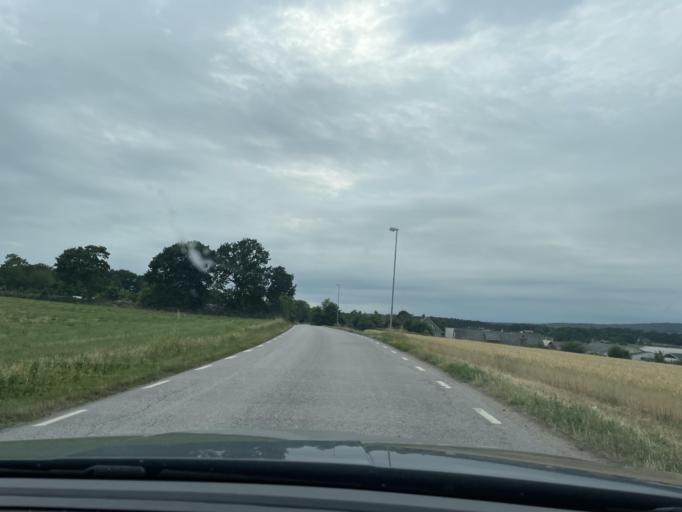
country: SE
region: Blekinge
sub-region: Solvesborgs Kommun
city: Soelvesborg
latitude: 56.0395
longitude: 14.6317
